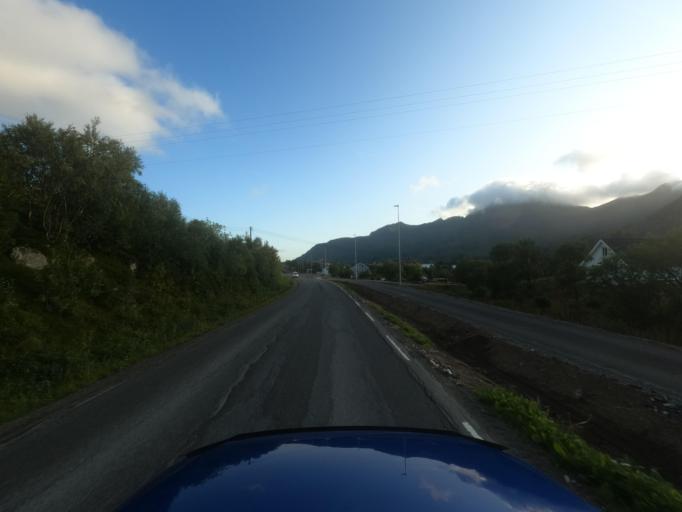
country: NO
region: Nordland
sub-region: Vestvagoy
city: Gravdal
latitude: 68.1003
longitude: 13.5470
